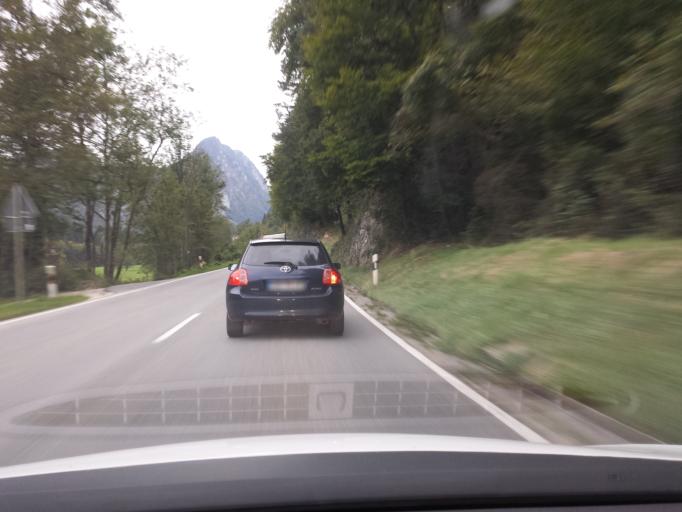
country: DE
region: Bavaria
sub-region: Upper Bavaria
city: Schneizlreuth
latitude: 47.6848
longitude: 12.7930
